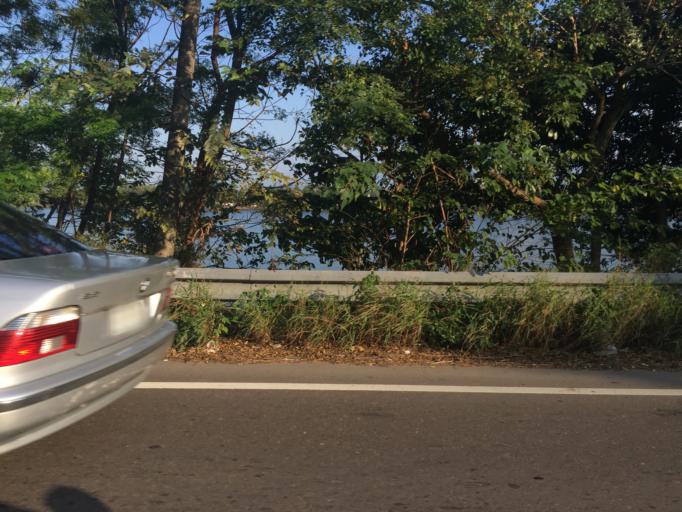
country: TW
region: Taiwan
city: Daxi
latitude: 24.9138
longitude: 121.2544
